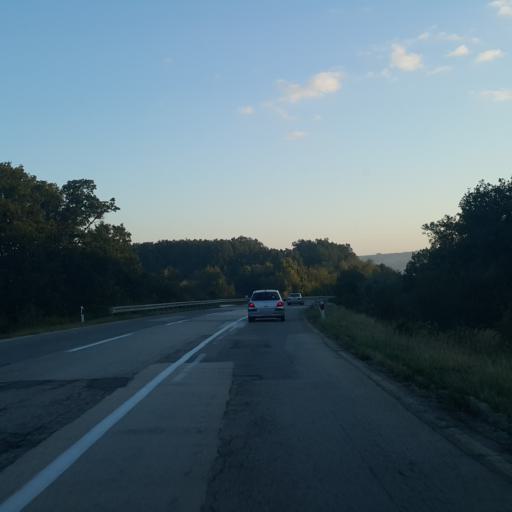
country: RS
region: Central Serbia
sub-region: Zajecarski Okrug
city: Zajecar
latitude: 44.0741
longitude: 22.3336
